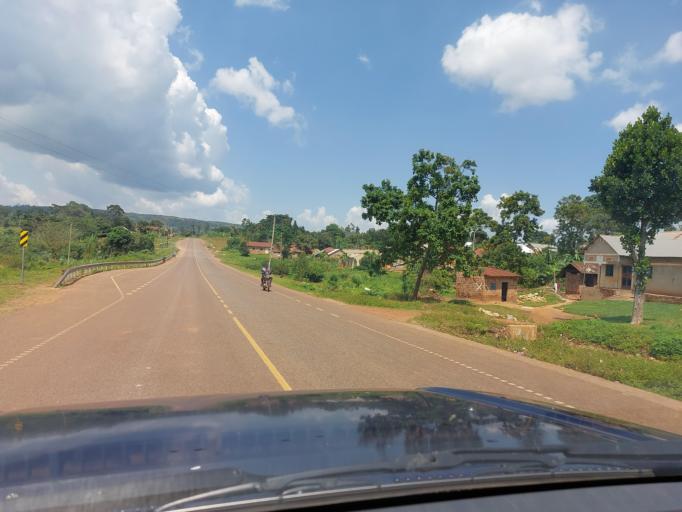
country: UG
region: Central Region
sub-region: Buikwe District
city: Buikwe
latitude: 0.3135
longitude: 33.1050
